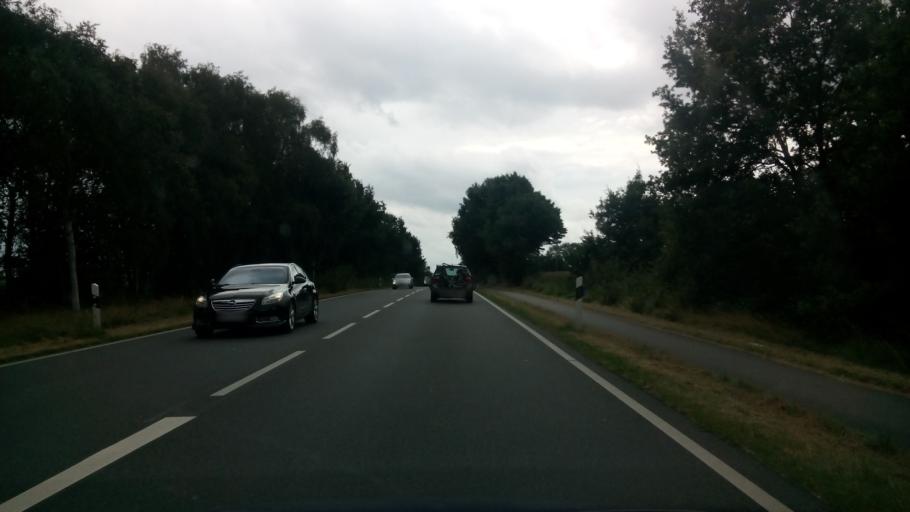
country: DE
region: Lower Saxony
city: Marl
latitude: 52.4899
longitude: 8.3662
